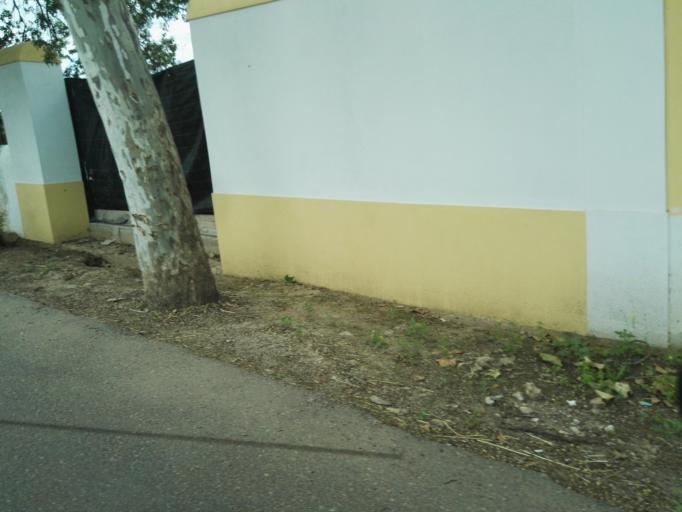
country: PT
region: Portalegre
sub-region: Elvas
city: Elvas
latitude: 38.8734
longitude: -7.1731
